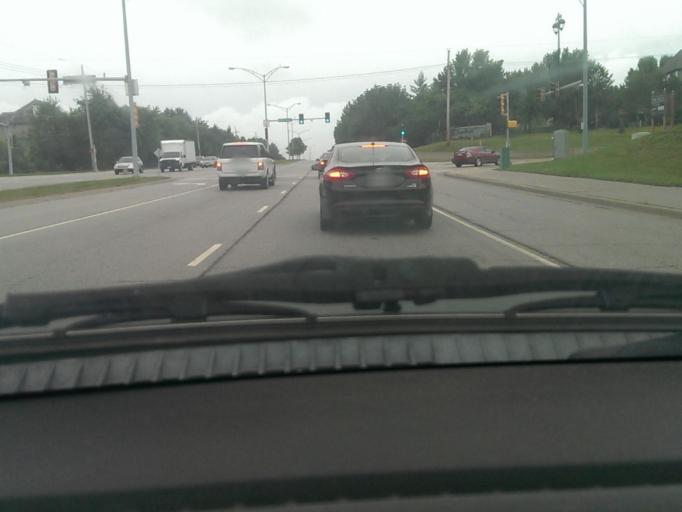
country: US
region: Kansas
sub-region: Johnson County
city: Leawood
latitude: 38.8989
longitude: -94.6493
